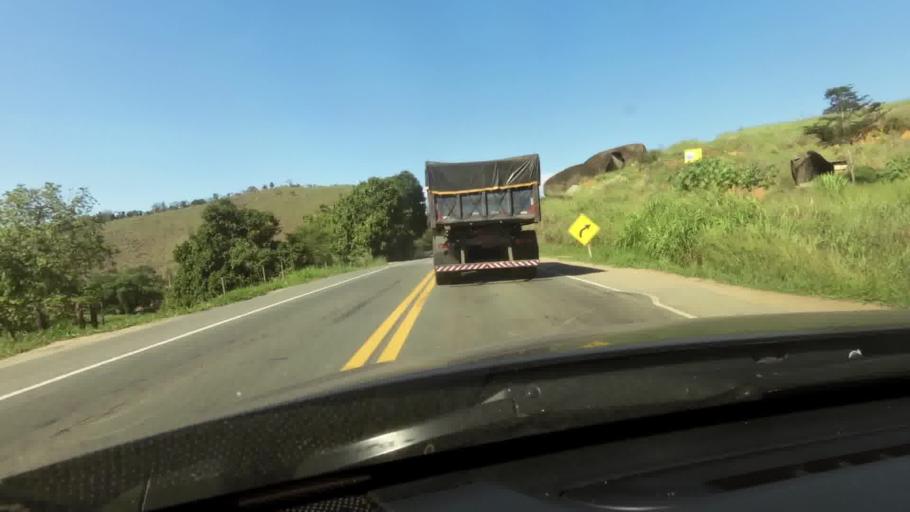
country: BR
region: Espirito Santo
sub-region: Cachoeiro De Itapemirim
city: Cachoeiro de Itapemirim
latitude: -20.9095
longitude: -41.0694
